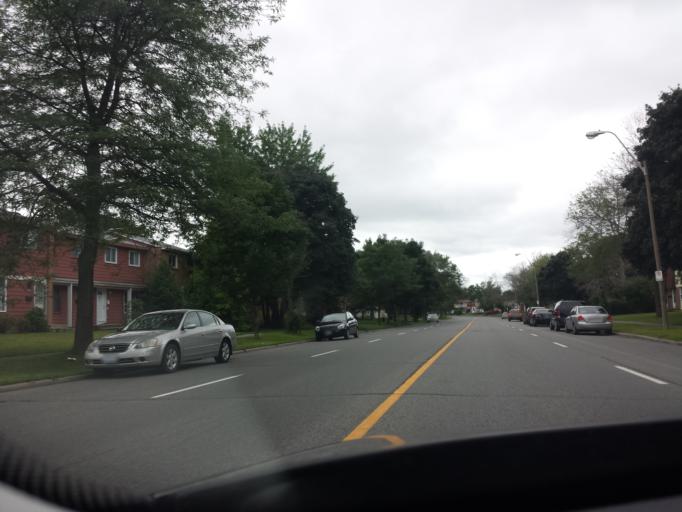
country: CA
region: Ontario
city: Ottawa
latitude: 45.3672
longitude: -75.7037
